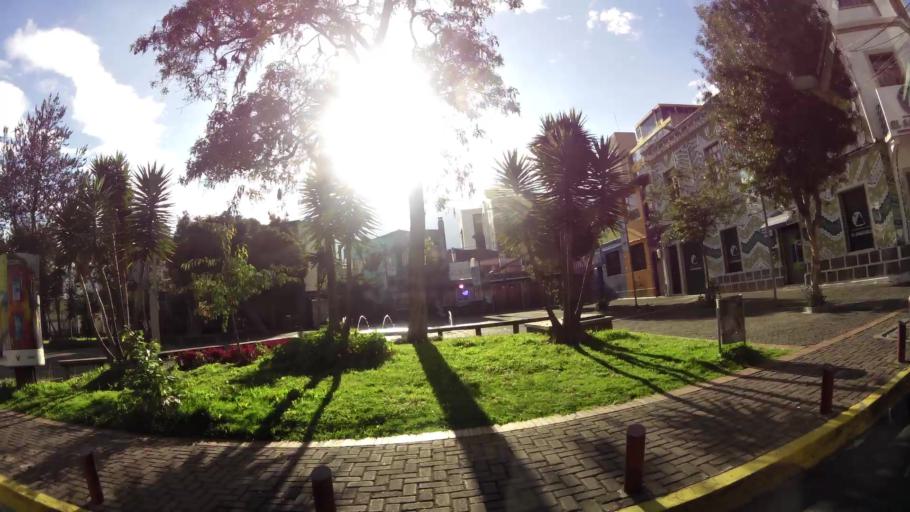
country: EC
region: Pichincha
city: Quito
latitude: -0.2031
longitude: -78.4955
